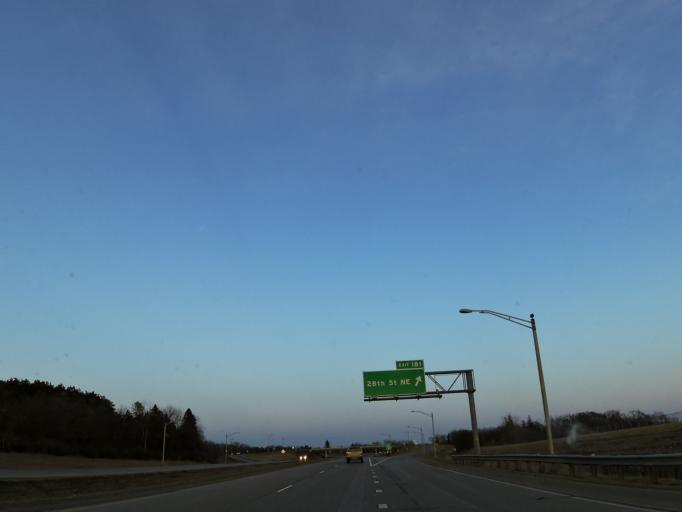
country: US
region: Minnesota
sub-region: Mower County
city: Austin
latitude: 43.6739
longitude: -92.9349
